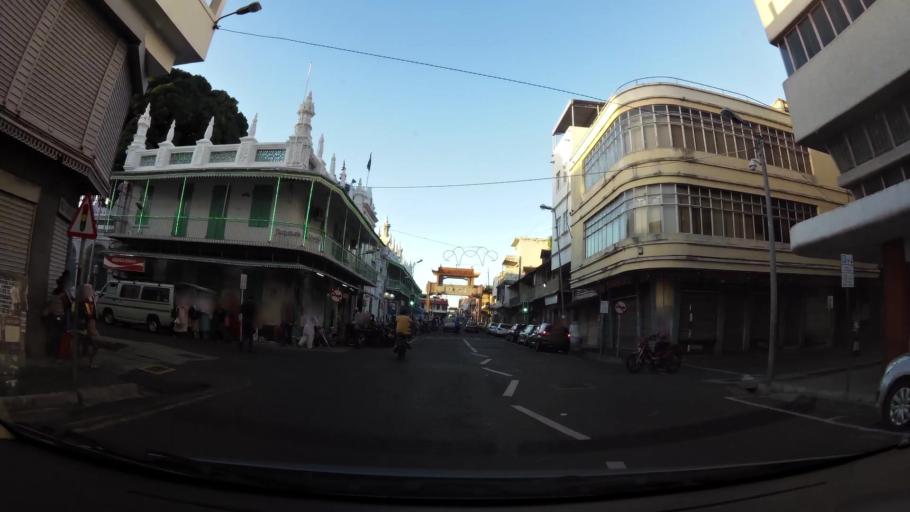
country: MU
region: Port Louis
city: Port Louis
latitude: -20.1603
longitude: 57.5051
